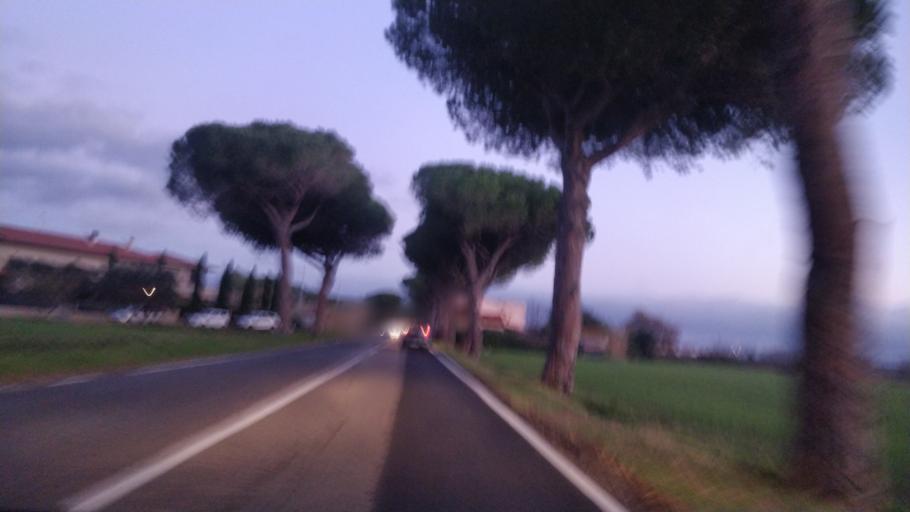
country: IT
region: Tuscany
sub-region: Provincia di Livorno
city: S.P. in Palazzi
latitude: 43.3330
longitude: 10.4953
